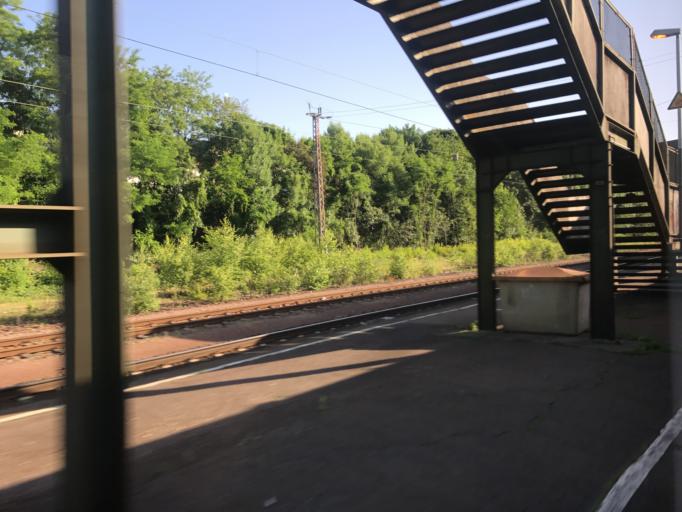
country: DE
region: Saarland
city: Friedrichsthal
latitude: 49.3194
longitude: 7.0882
